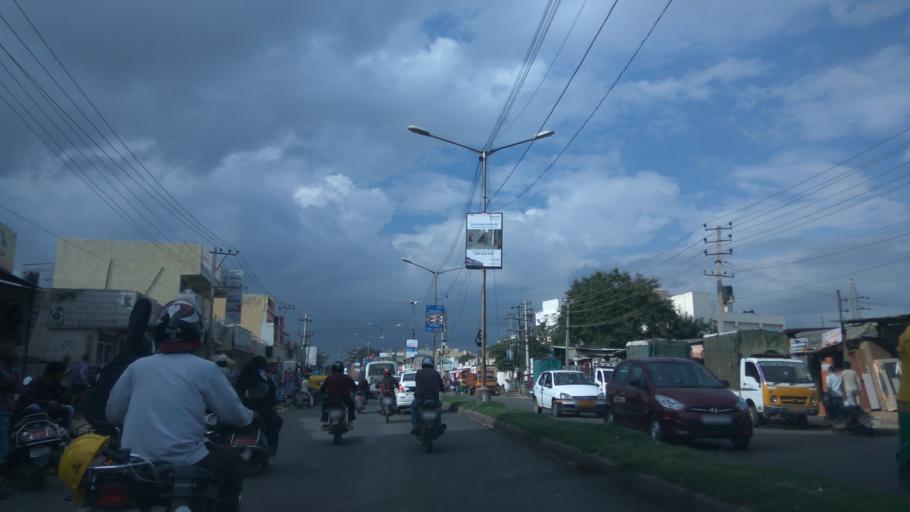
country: IN
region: Karnataka
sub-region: Bangalore Urban
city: Yelahanka
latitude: 13.0486
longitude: 77.6293
